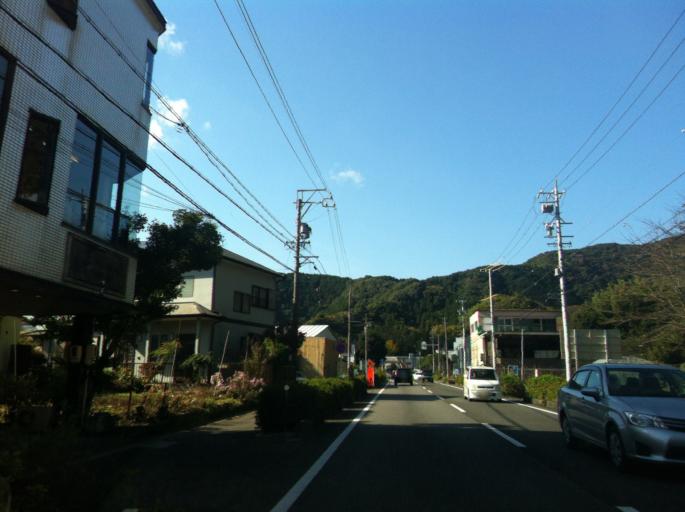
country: JP
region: Shizuoka
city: Shizuoka-shi
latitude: 34.9510
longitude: 138.3376
